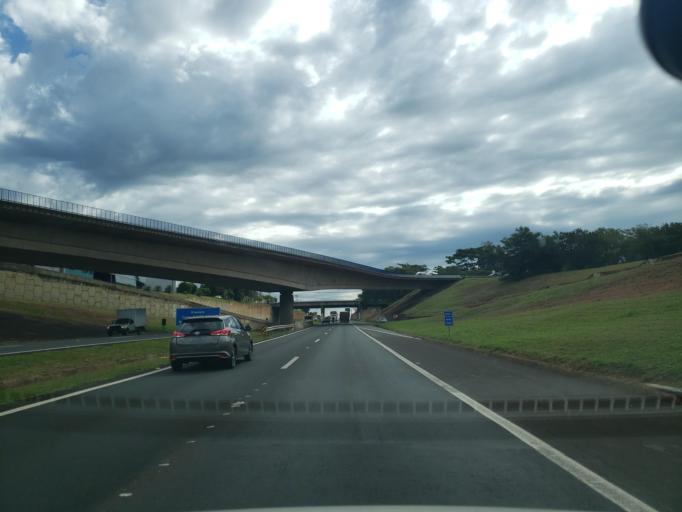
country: BR
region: Sao Paulo
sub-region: Bauru
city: Bauru
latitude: -22.2952
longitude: -49.0709
